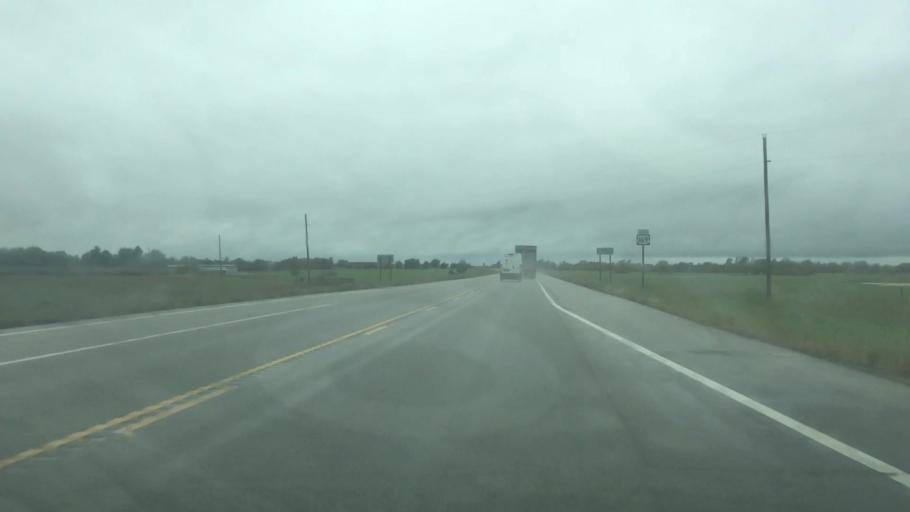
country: US
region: Kansas
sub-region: Allen County
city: Iola
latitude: 38.0812
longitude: -95.3707
